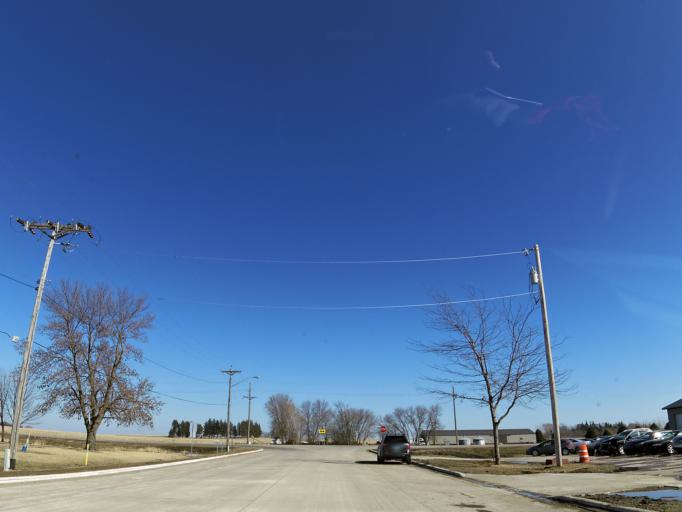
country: US
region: Minnesota
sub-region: Waseca County
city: New Richland
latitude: 43.8971
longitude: -93.4877
